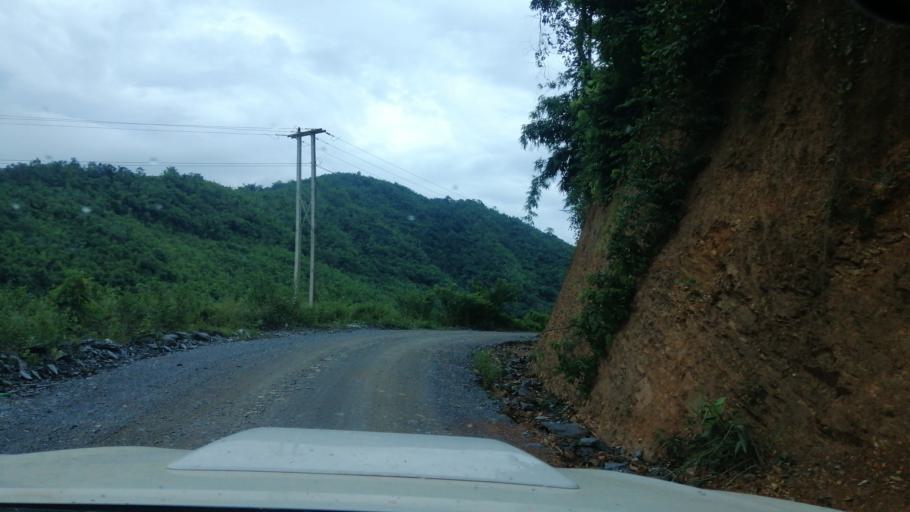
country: LA
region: Xiagnabouli
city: Sainyabuli
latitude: 19.1830
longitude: 101.7971
